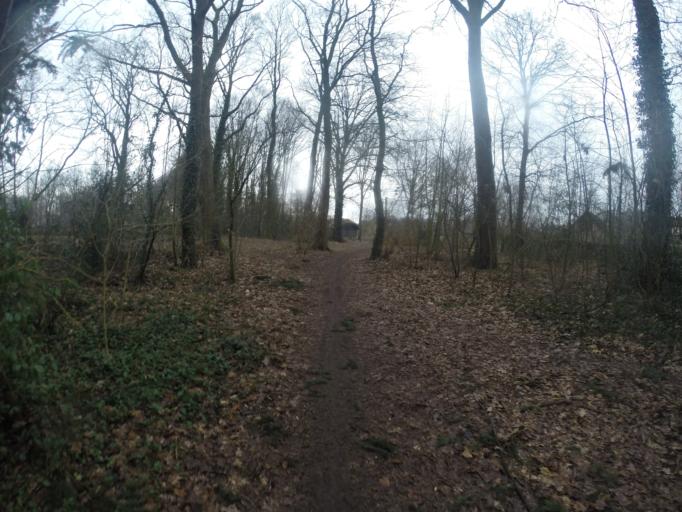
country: NL
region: Gelderland
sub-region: Gemeente Bronckhorst
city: Zelhem
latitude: 52.0081
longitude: 6.3600
